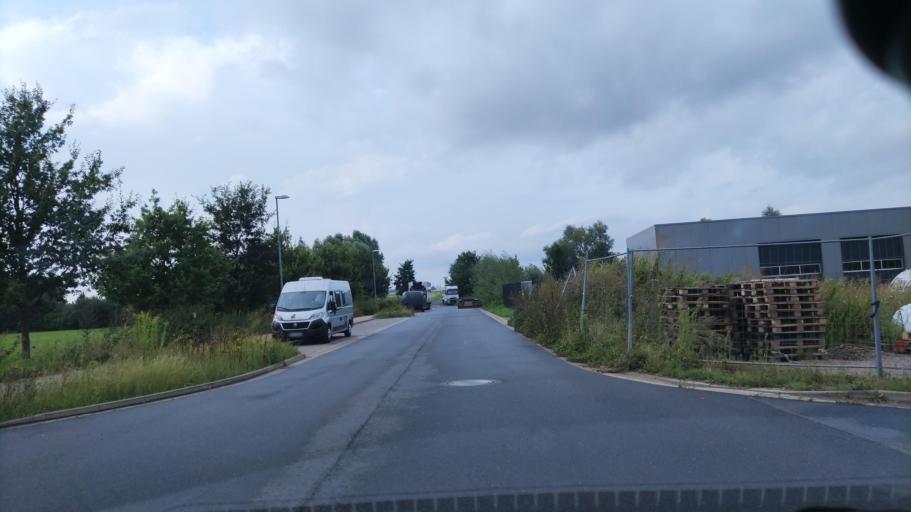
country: DE
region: Lower Saxony
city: Sarstedt
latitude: 52.2751
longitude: 9.8507
